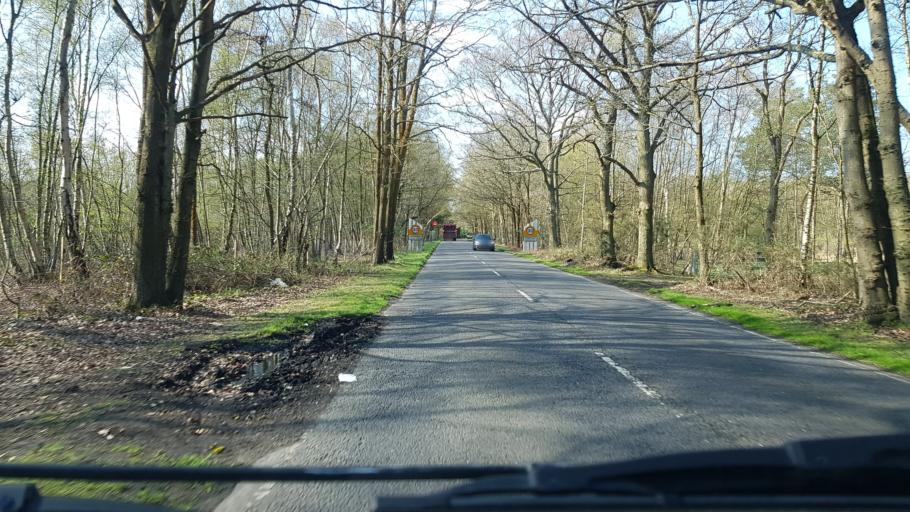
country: GB
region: England
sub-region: Surrey
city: Pirbright
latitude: 51.2971
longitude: -0.6372
